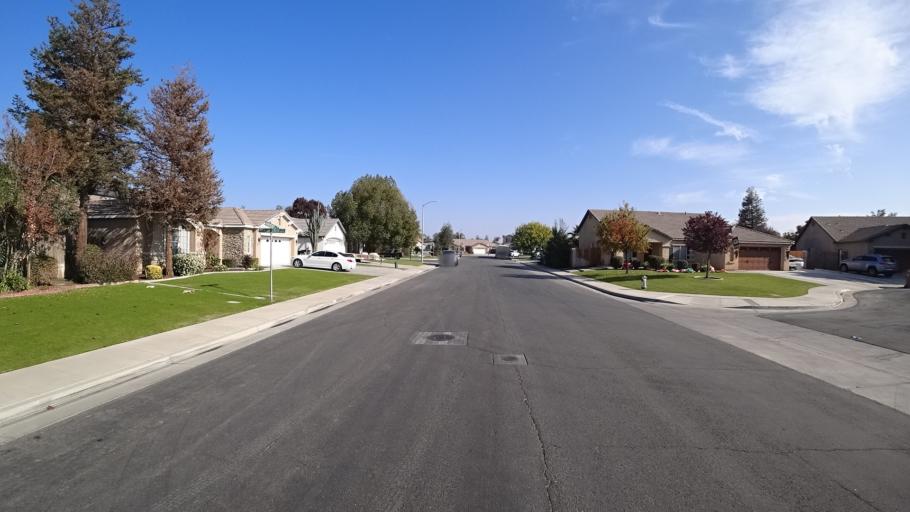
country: US
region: California
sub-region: Kern County
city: Rosedale
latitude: 35.3594
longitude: -119.1704
